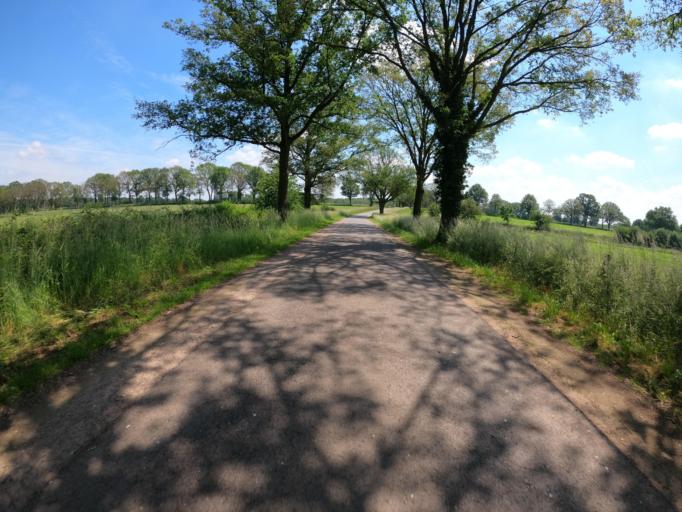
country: DE
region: North Rhine-Westphalia
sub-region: Regierungsbezirk Dusseldorf
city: Schermbeck
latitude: 51.6901
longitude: 6.8355
